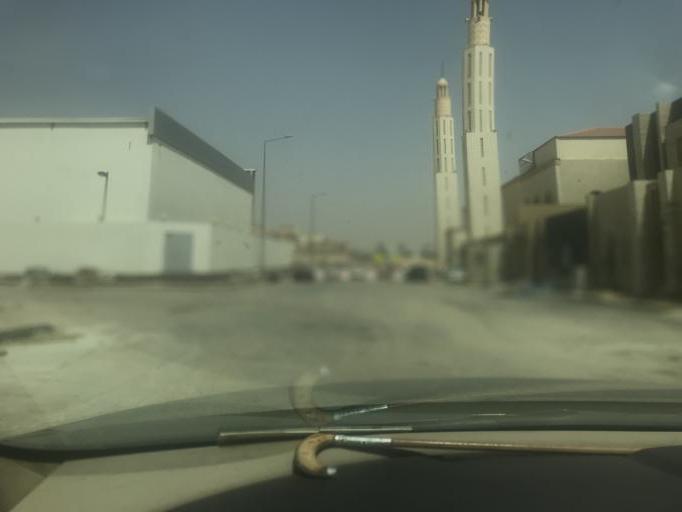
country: SA
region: Ar Riyad
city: Riyadh
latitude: 24.8204
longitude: 46.6025
